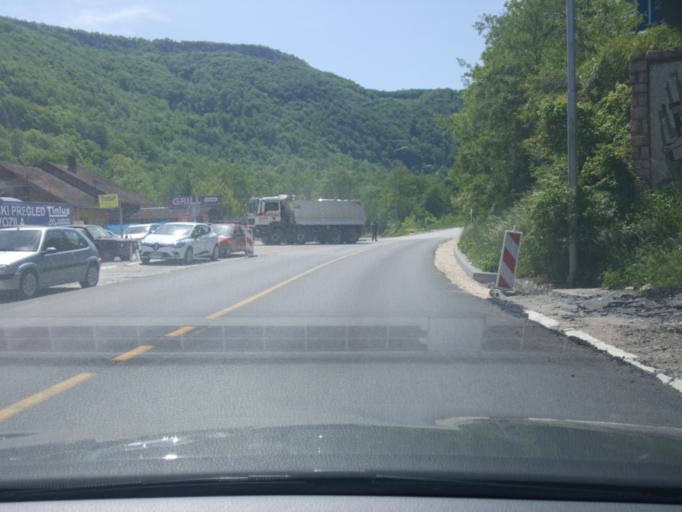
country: RS
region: Central Serbia
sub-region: Zlatiborski Okrug
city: Uzice
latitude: 43.8361
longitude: 19.8822
